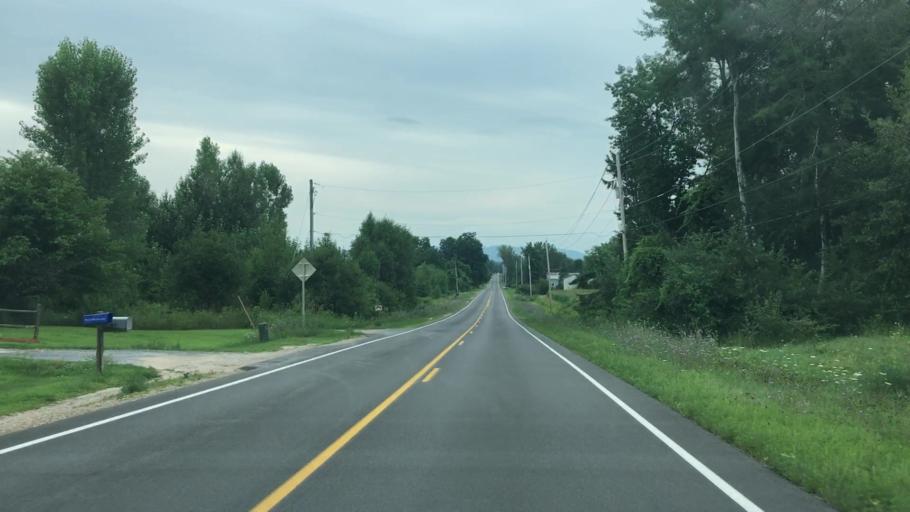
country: US
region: New York
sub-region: Clinton County
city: Peru
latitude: 44.5959
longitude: -73.5732
